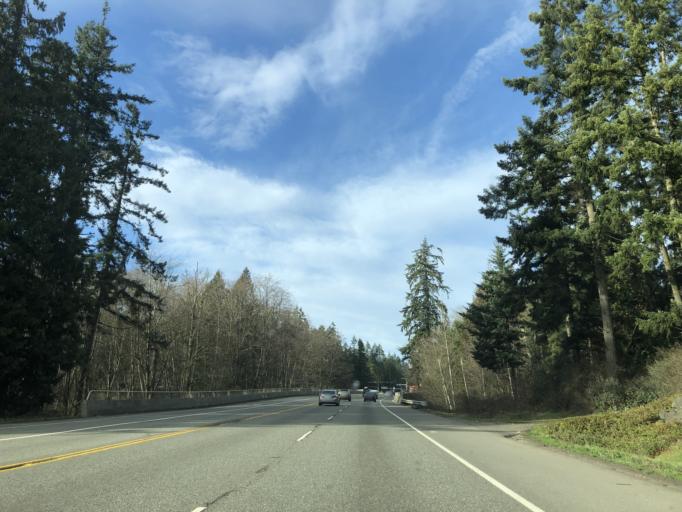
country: US
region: Washington
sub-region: Kitsap County
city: Poulsbo
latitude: 47.7546
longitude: -122.6492
